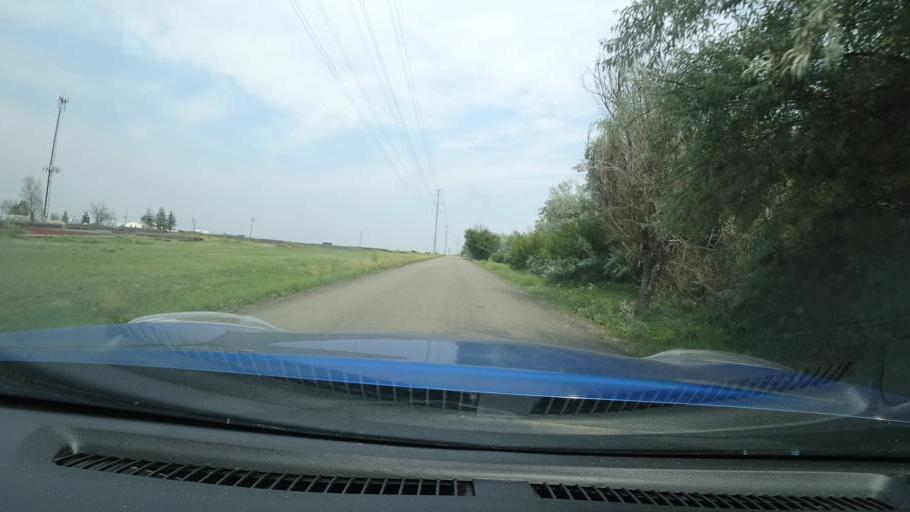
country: US
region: Colorado
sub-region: Adams County
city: Aurora
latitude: 39.7547
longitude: -104.7513
